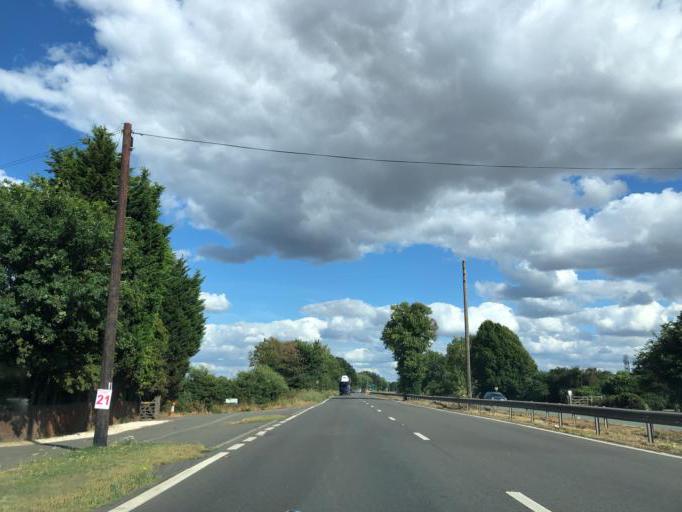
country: GB
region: England
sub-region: Warwickshire
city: Wolston
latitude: 52.3478
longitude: -1.3512
